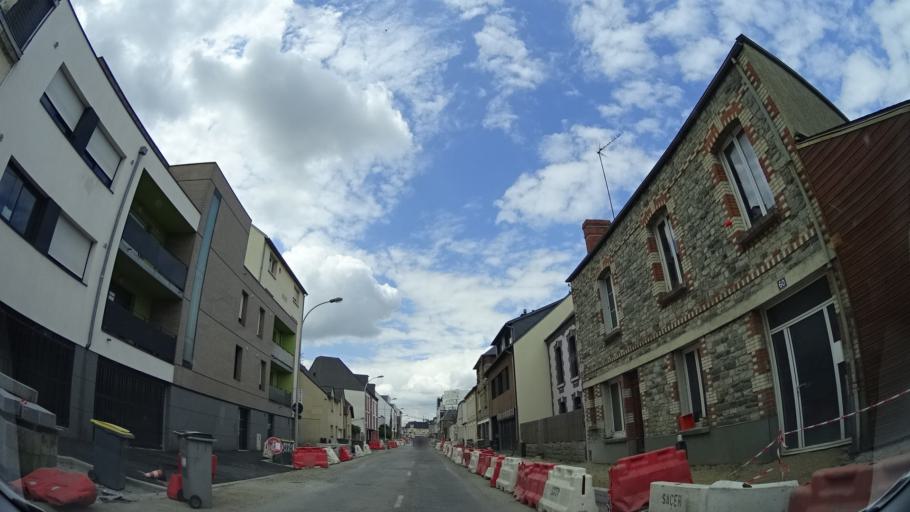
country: FR
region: Brittany
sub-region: Departement d'Ille-et-Vilaine
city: Rennes
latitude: 48.1086
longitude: -1.7046
